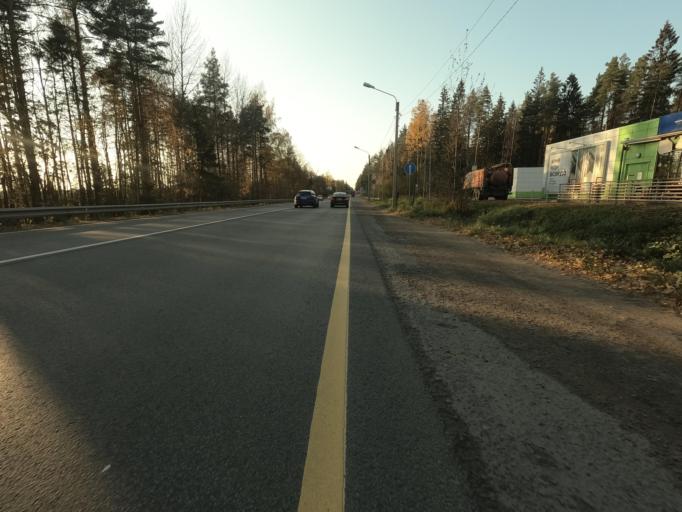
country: RU
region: St.-Petersburg
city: Pesochnyy
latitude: 60.1802
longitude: 30.1384
